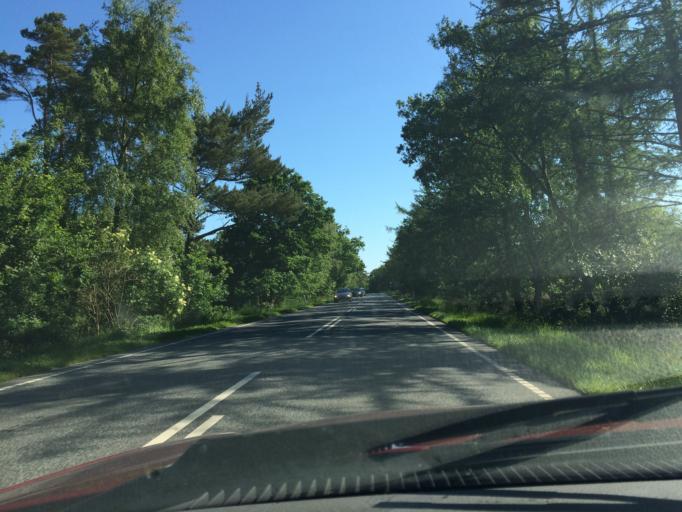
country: DK
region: Central Jutland
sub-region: Viborg Kommune
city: Bjerringbro
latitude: 56.3042
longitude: 9.6854
